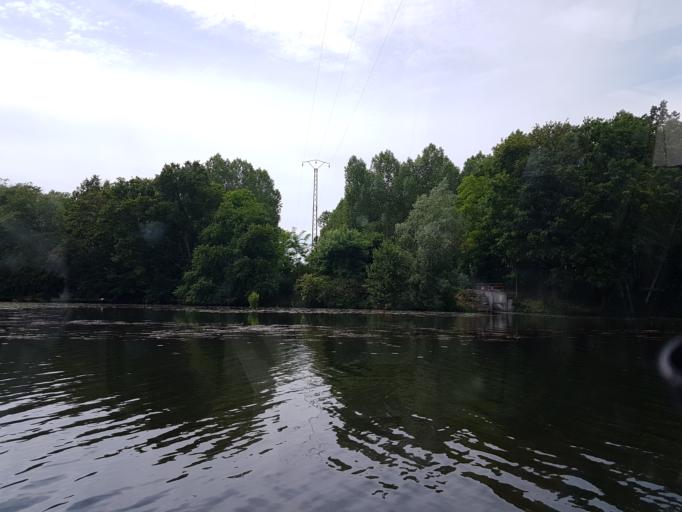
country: FR
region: Bourgogne
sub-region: Departement de l'Yonne
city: Gurgy
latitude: 47.8629
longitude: 3.5523
